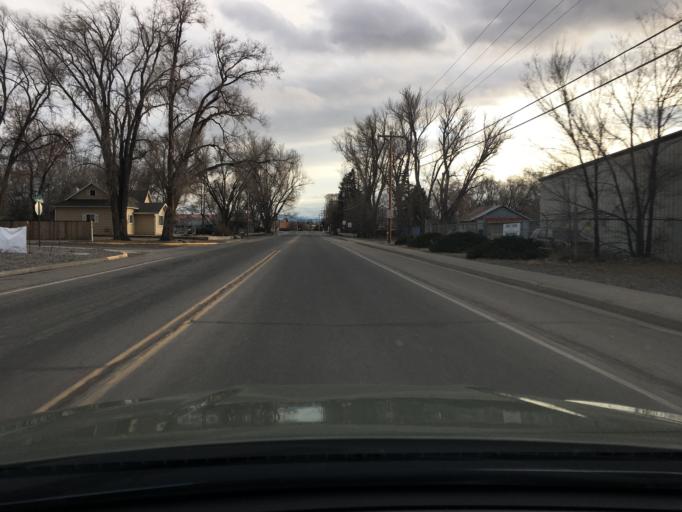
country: US
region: Colorado
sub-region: Montrose County
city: Montrose
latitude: 38.4859
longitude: -107.8571
